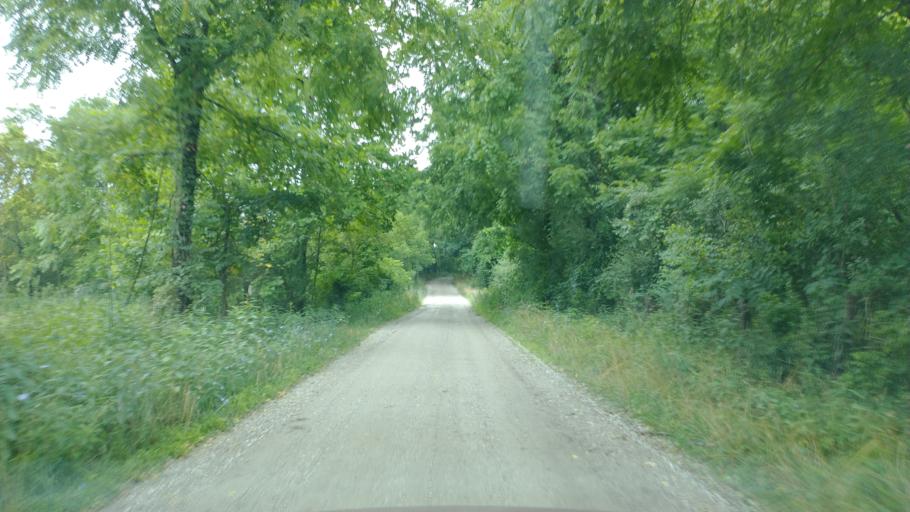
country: US
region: Ohio
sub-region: Meigs County
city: Middleport
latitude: 38.9276
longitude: -82.0599
